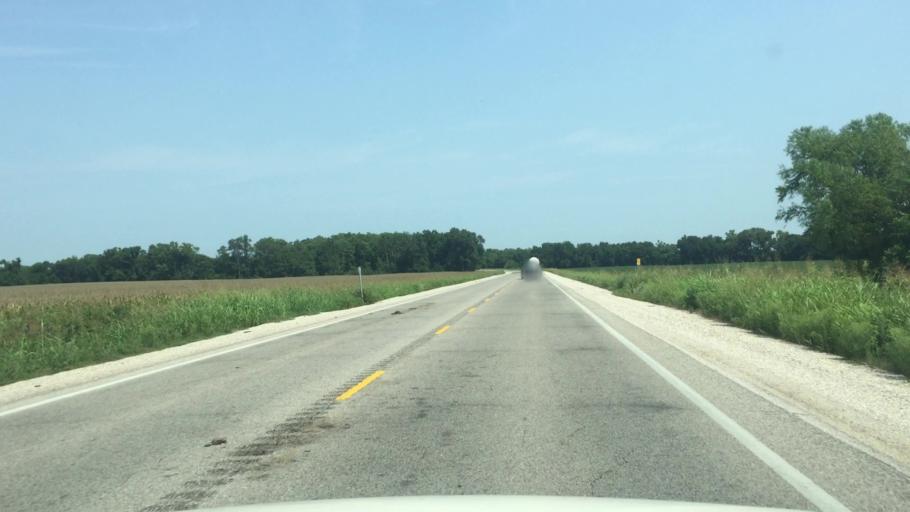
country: US
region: Kansas
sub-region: Montgomery County
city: Cherryvale
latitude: 37.1721
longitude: -95.5764
